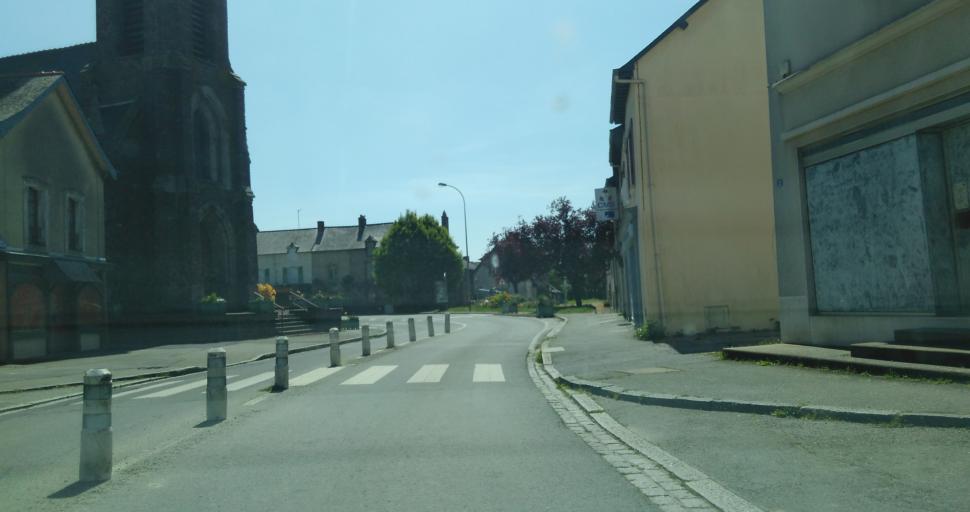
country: FR
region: Brittany
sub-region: Departement d'Ille-et-Vilaine
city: Saint-Gilles
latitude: 48.1262
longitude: -1.8181
